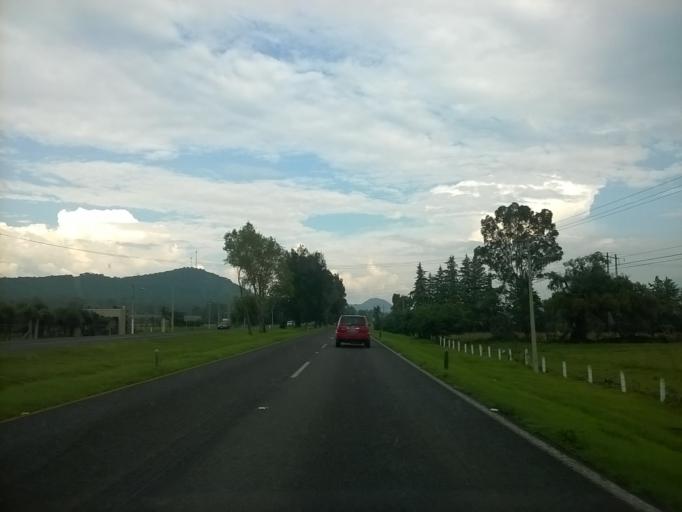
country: MX
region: Michoacan
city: Cuanajo
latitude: 19.5335
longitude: -101.4996
